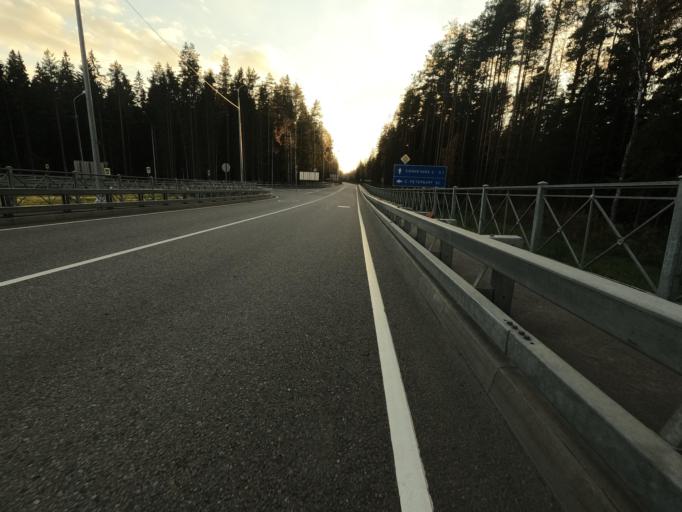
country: RU
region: St.-Petersburg
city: Solnechnoye
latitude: 60.1686
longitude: 29.9681
